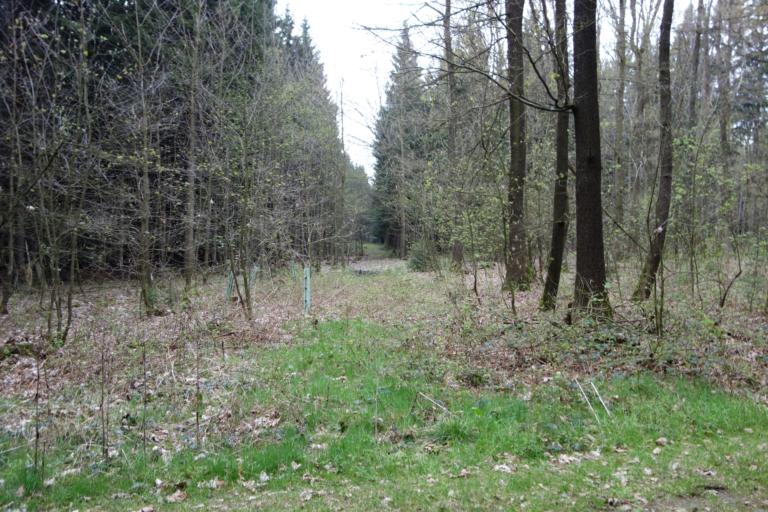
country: DE
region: Saxony
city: Eppendorf
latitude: 50.8319
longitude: 13.2603
